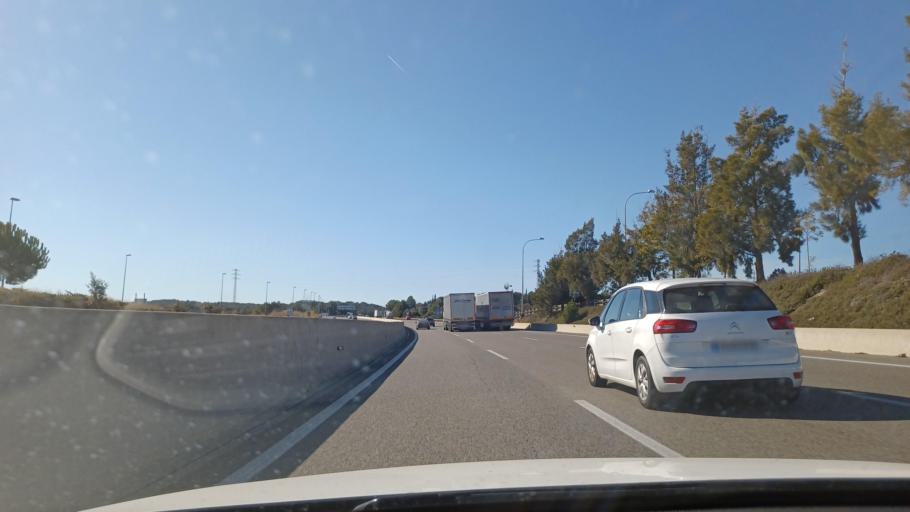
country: ES
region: Catalonia
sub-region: Provincia de Tarragona
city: Torredembarra
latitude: 41.1588
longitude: 1.3906
